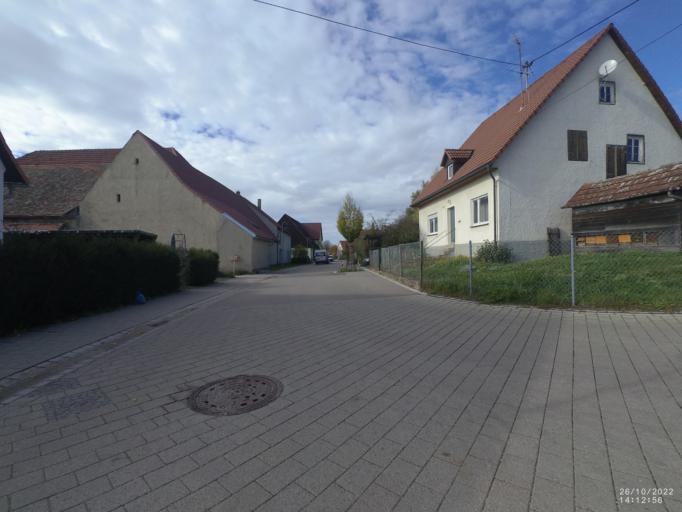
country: DE
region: Baden-Wuerttemberg
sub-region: Regierungsbezirk Stuttgart
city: Geislingen an der Steige
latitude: 48.6511
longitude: 9.8634
